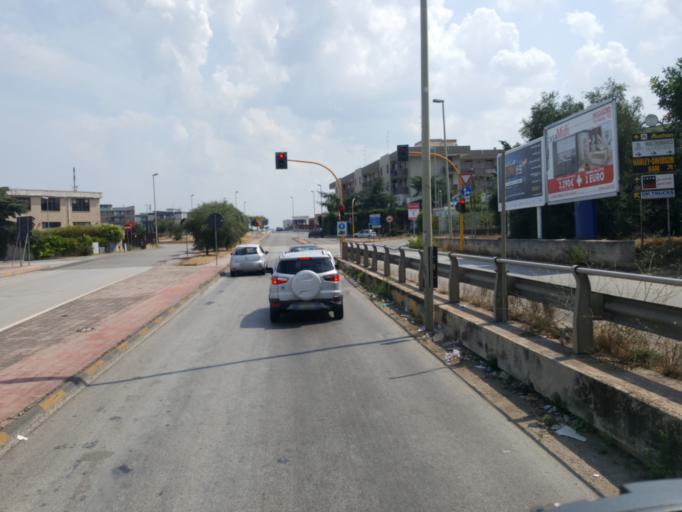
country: IT
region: Apulia
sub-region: Provincia di Bari
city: Modugno
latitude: 41.0910
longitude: 16.7778
